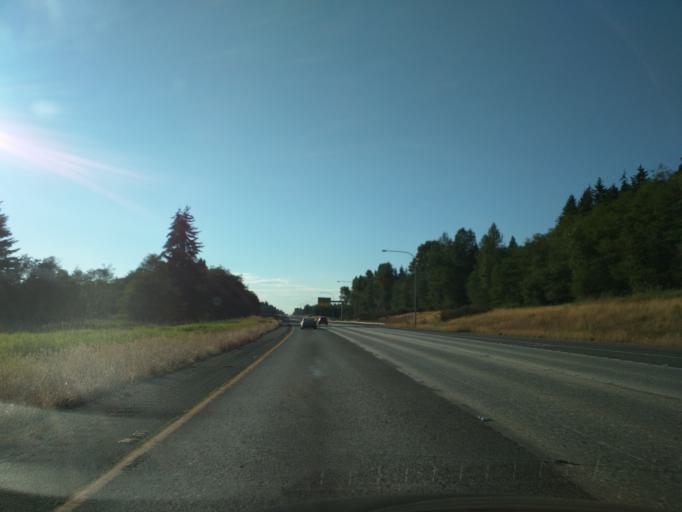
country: US
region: Washington
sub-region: Snohomish County
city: Bryant
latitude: 48.2613
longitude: -122.2610
